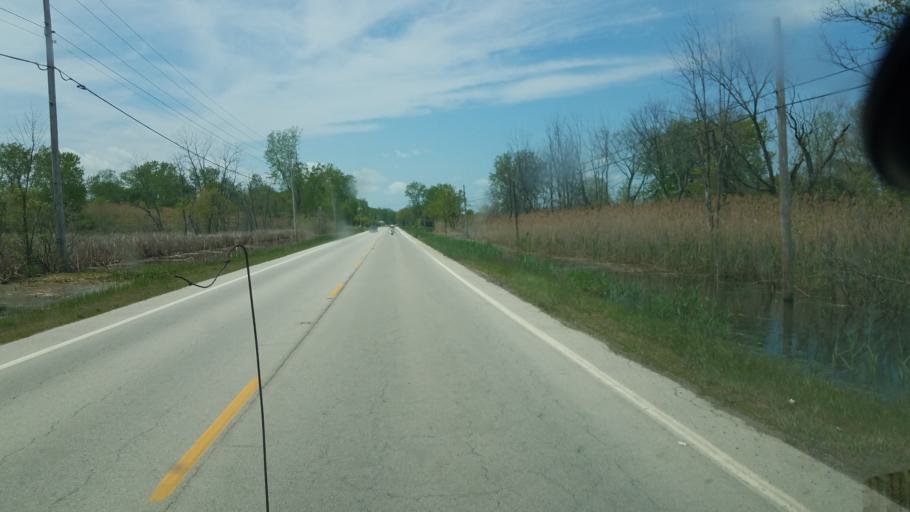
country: US
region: Ohio
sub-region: Ottawa County
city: Port Clinton
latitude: 41.5209
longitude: -82.9823
